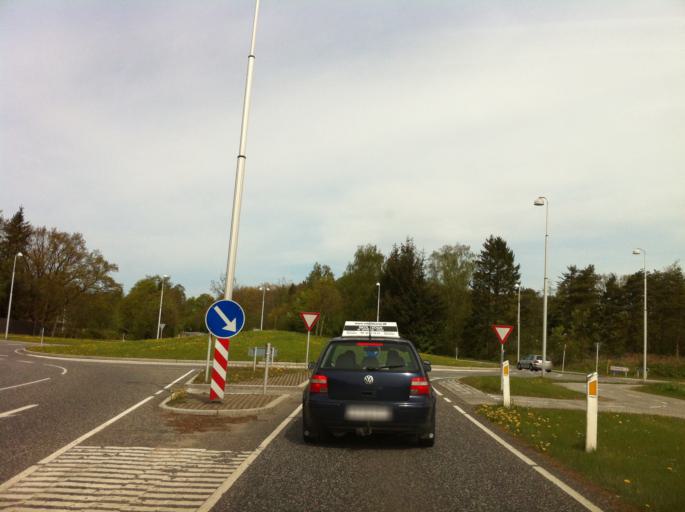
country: DK
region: Capital Region
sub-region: Allerod Kommune
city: Blovstrod
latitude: 55.8936
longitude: 12.3697
